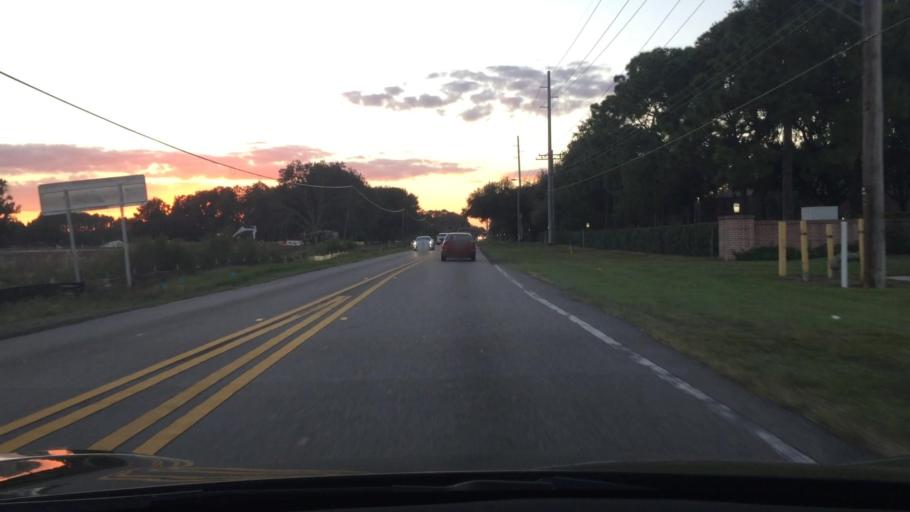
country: US
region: Florida
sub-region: Hillsborough County
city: Greater Northdale
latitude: 28.1280
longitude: -82.5355
